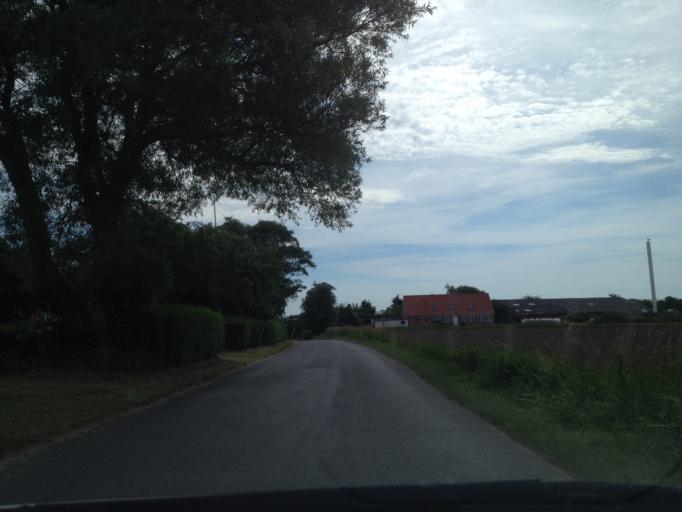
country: DK
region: Central Jutland
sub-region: Samso Kommune
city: Tranebjerg
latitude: 55.9663
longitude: 10.5477
